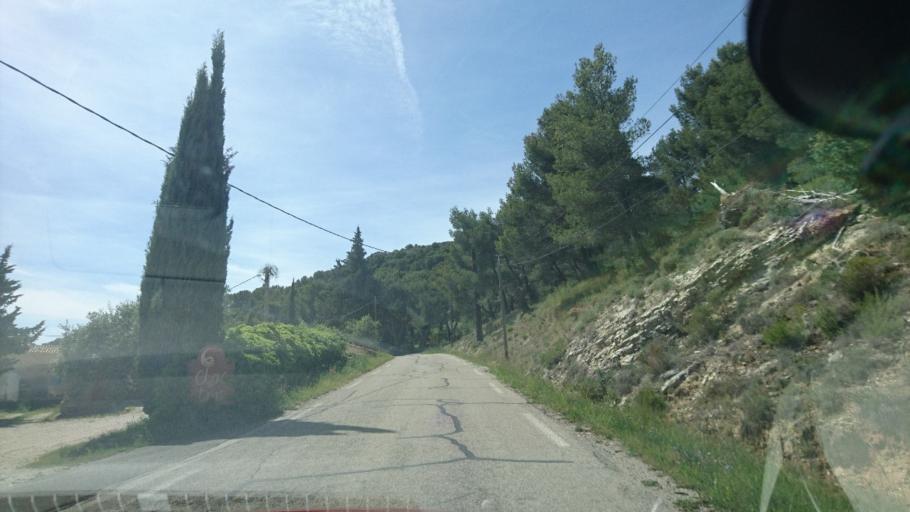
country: FR
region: Provence-Alpes-Cote d'Azur
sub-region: Departement du Vaucluse
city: Caromb
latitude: 44.1433
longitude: 5.0903
